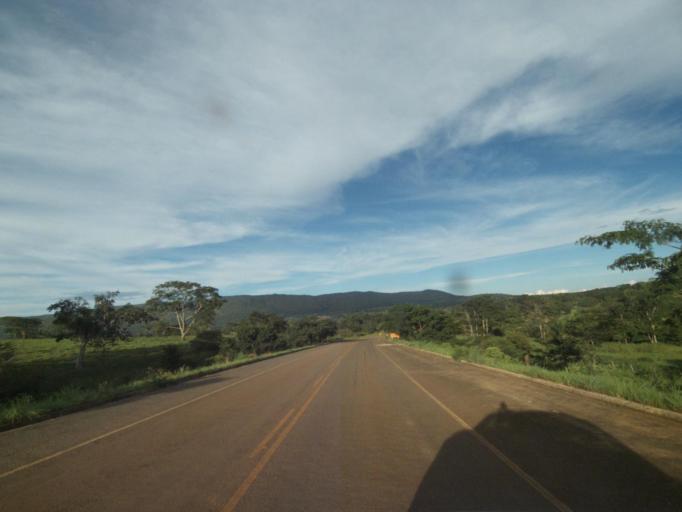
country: BR
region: Goias
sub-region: Jaragua
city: Jaragua
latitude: -15.8442
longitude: -49.3641
